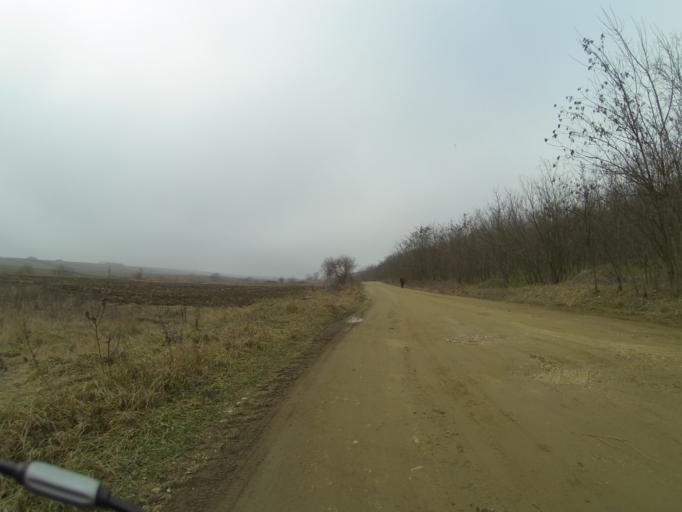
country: RO
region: Mehedinti
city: Padina Mica
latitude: 44.4864
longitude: 23.0239
